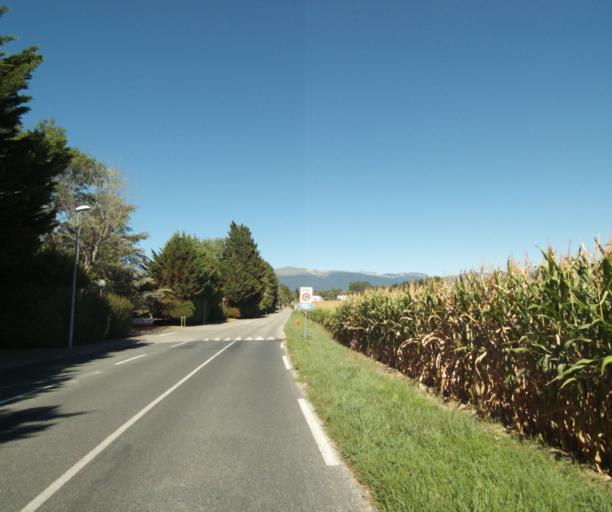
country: FR
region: Rhone-Alpes
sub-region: Departement de l'Ain
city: Ferney-Voltaire
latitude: 46.2599
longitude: 6.0996
